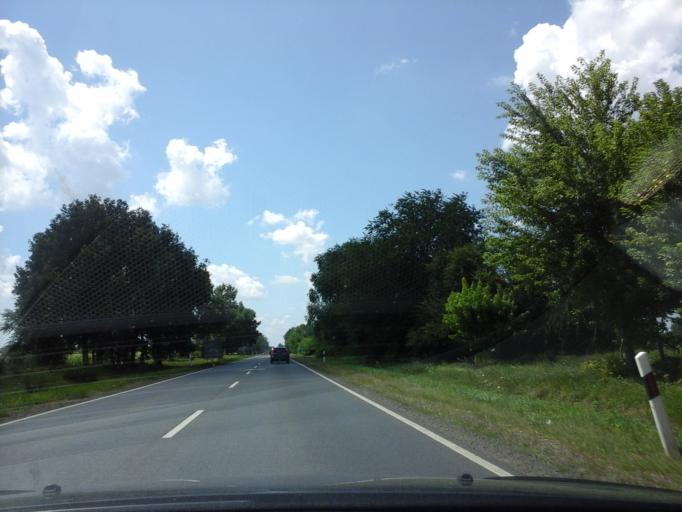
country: HU
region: Hajdu-Bihar
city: Ebes
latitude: 47.4806
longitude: 21.4973
